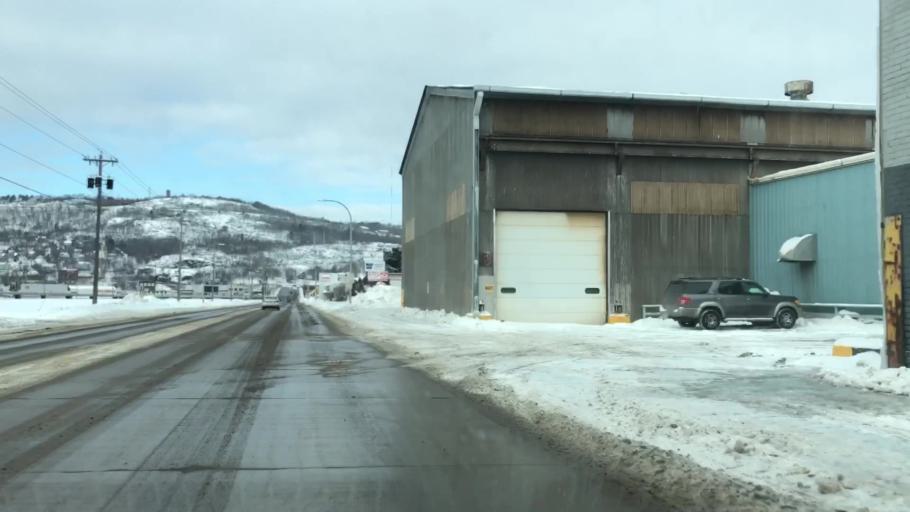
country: US
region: Minnesota
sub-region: Saint Louis County
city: Duluth
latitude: 46.7645
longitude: -92.1128
